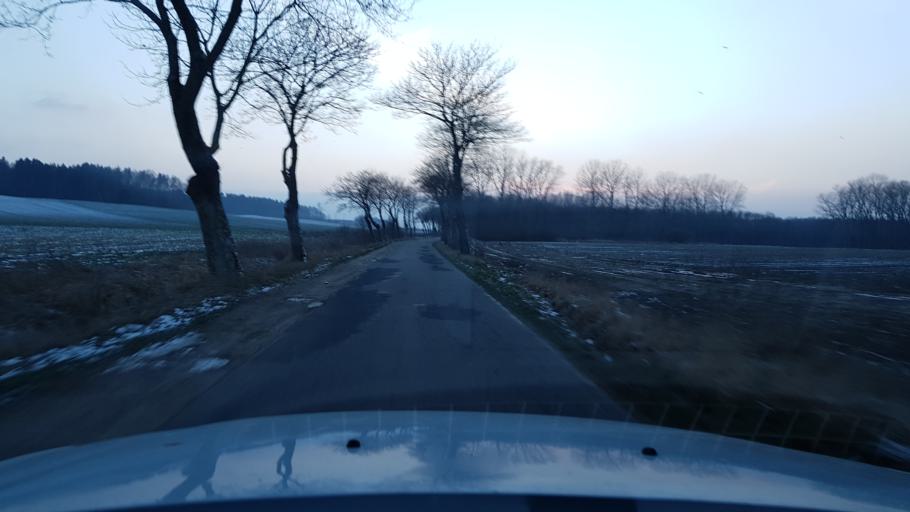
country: PL
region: West Pomeranian Voivodeship
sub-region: Powiat bialogardzki
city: Karlino
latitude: 53.9937
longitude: 15.8220
